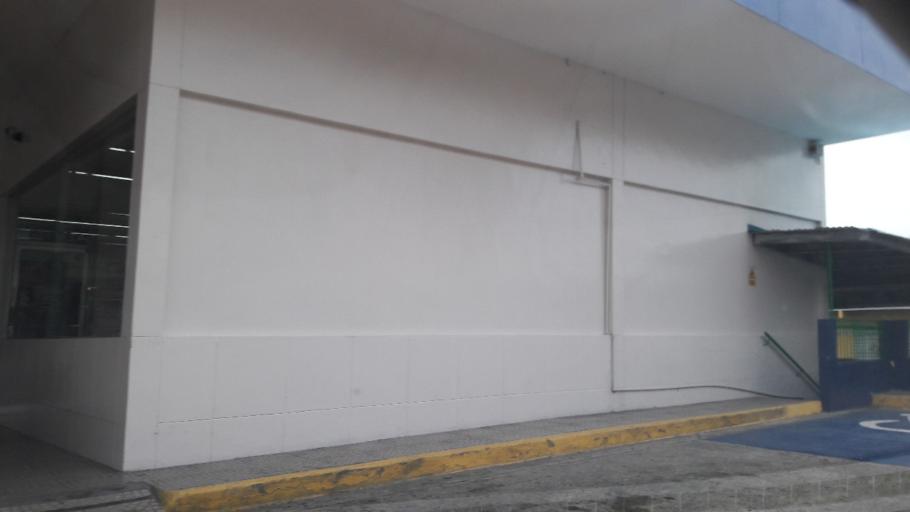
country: PA
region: Panama
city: Panama
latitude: 9.0135
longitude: -79.5255
